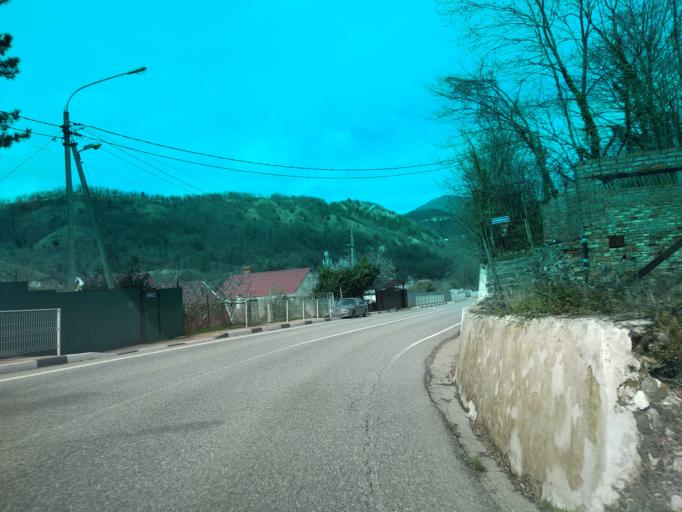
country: RU
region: Krasnodarskiy
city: Shepsi
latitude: 44.0560
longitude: 39.1344
